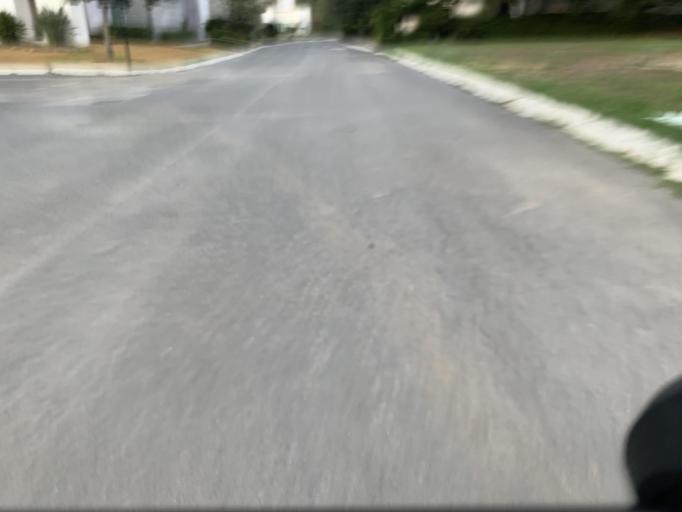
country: MX
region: Nuevo Leon
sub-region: Juarez
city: Bosques de San Pedro
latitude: 25.5186
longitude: -100.1962
